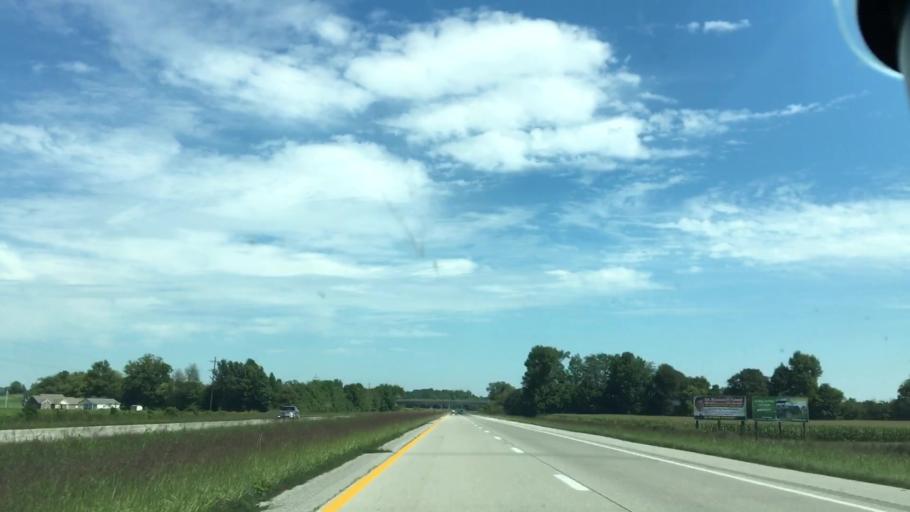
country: US
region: Kentucky
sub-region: Daviess County
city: Owensboro
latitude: 37.7657
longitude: -87.2176
